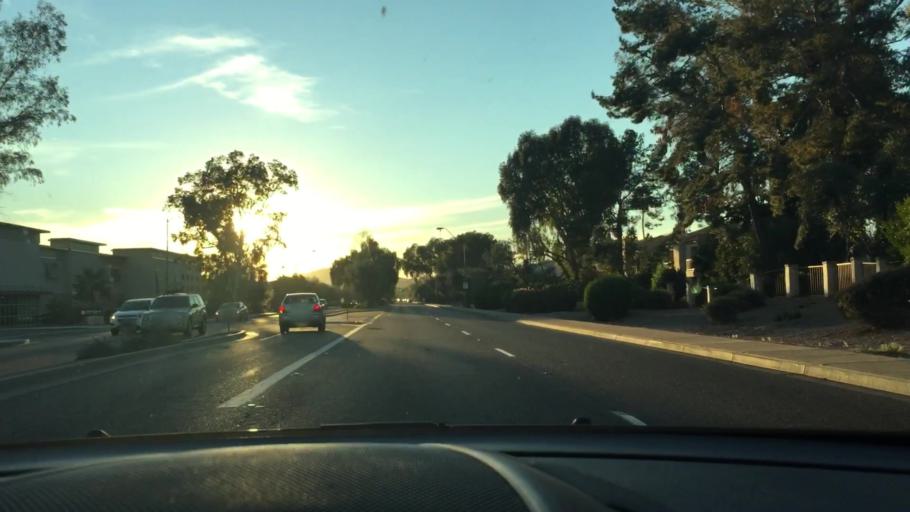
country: US
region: Arizona
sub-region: Maricopa County
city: Scottsdale
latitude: 33.5713
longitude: -111.8788
